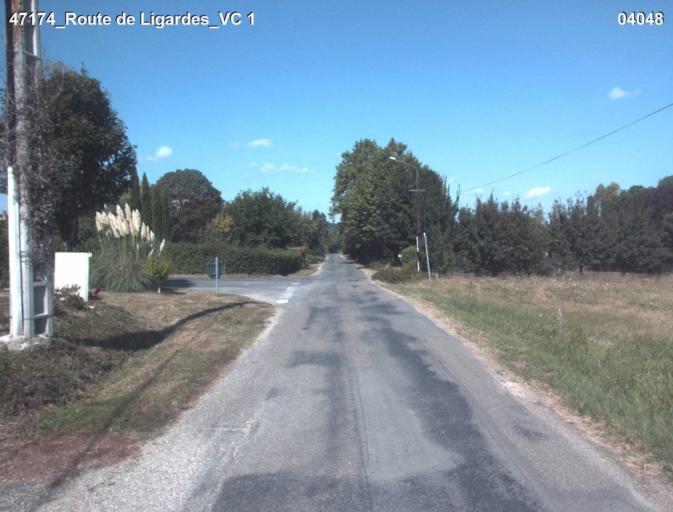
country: FR
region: Midi-Pyrenees
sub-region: Departement du Gers
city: Condom
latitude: 44.0339
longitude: 0.3736
